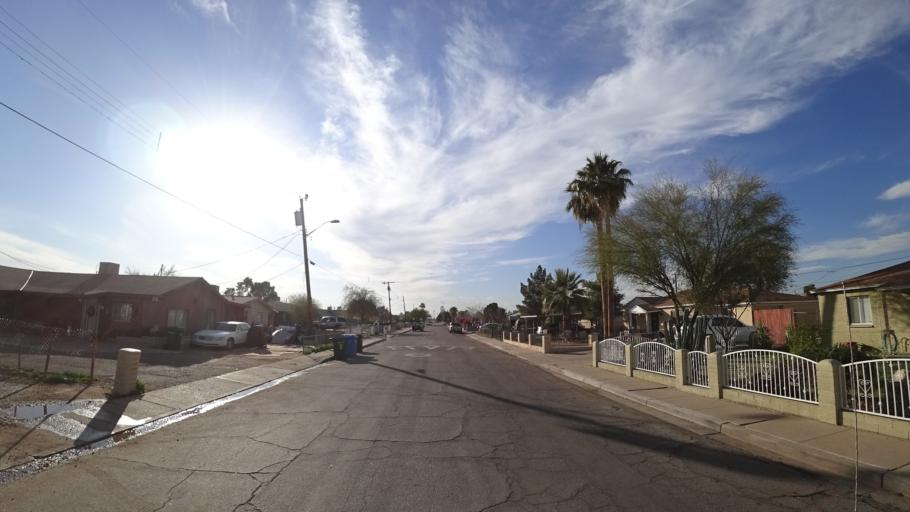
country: US
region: Arizona
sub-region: Maricopa County
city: Phoenix
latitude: 33.4549
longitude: -112.1244
